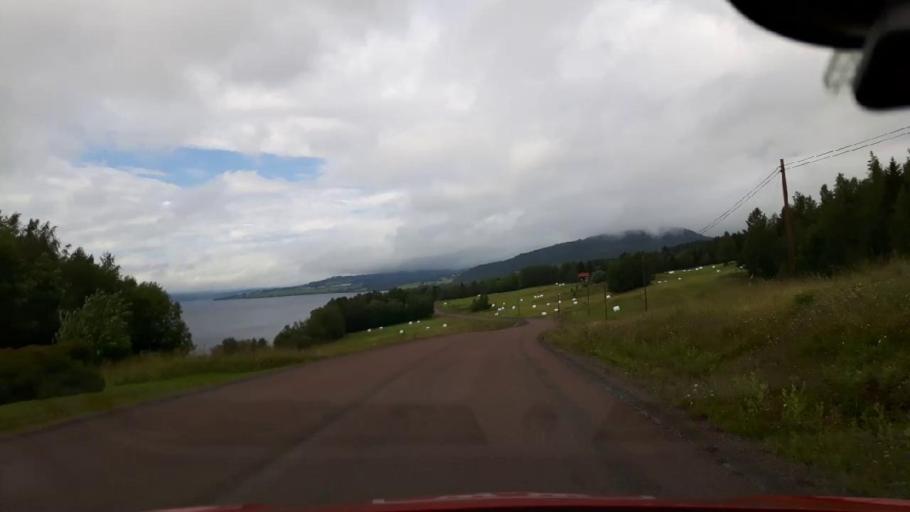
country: SE
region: Jaemtland
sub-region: Krokoms Kommun
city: Valla
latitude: 63.3673
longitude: 14.0498
